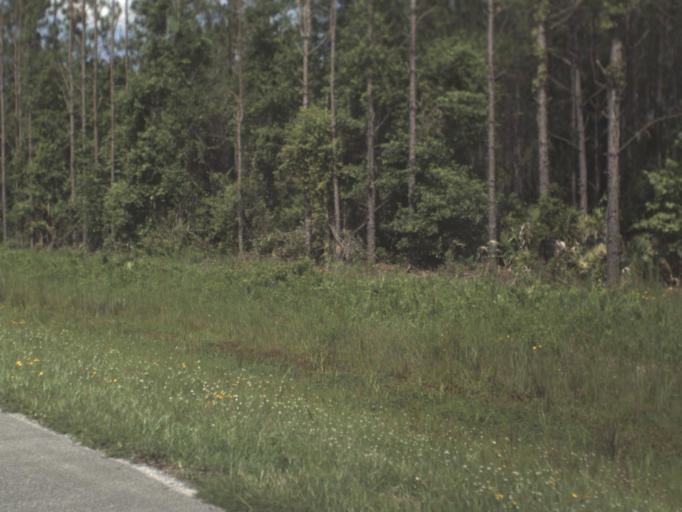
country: US
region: Florida
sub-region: Levy County
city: Bronson
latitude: 29.3900
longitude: -82.7029
